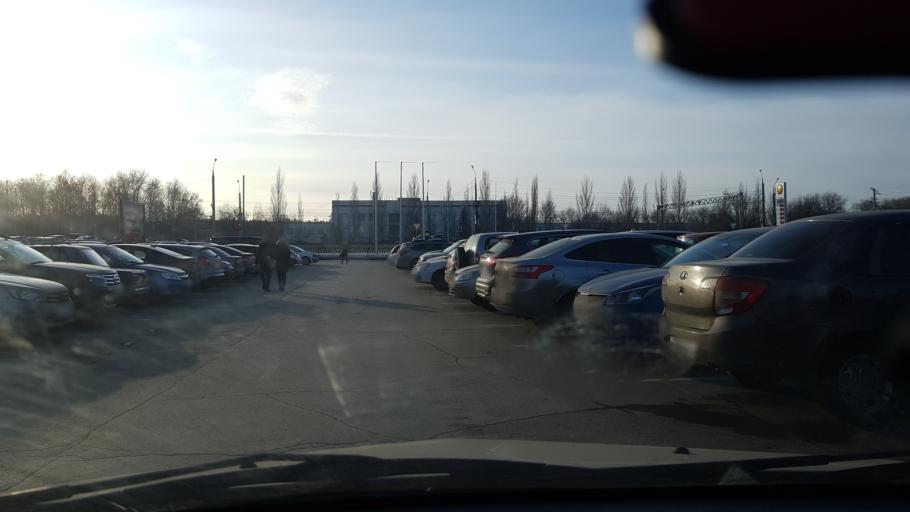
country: RU
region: Samara
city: Tol'yatti
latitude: 53.5415
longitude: 49.3882
